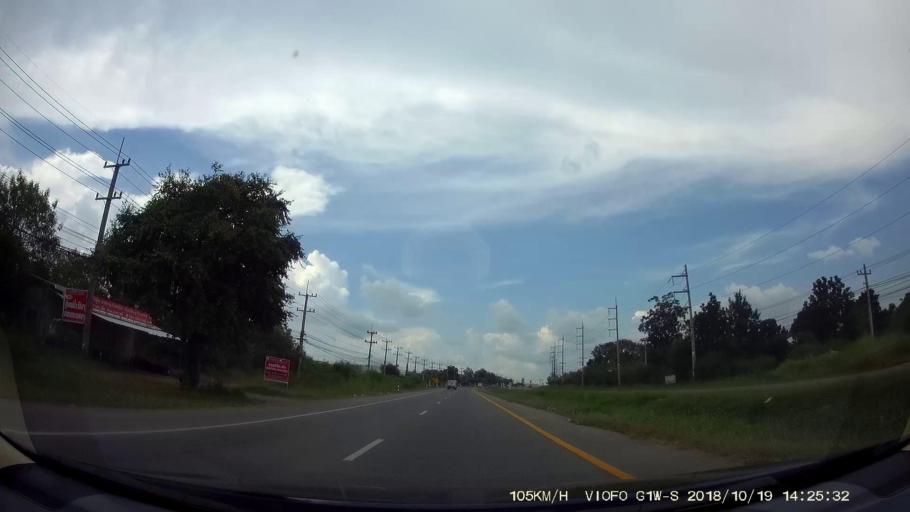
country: TH
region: Chaiyaphum
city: Kaeng Khro
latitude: 16.0951
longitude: 102.2641
